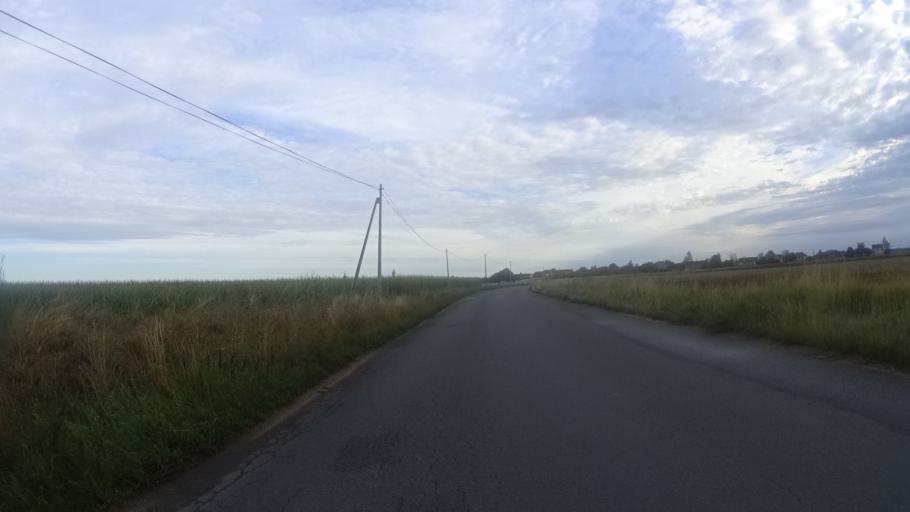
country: FR
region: Centre
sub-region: Departement du Loiret
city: Saint-Benoit-sur-Loire
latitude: 47.7966
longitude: 2.3114
